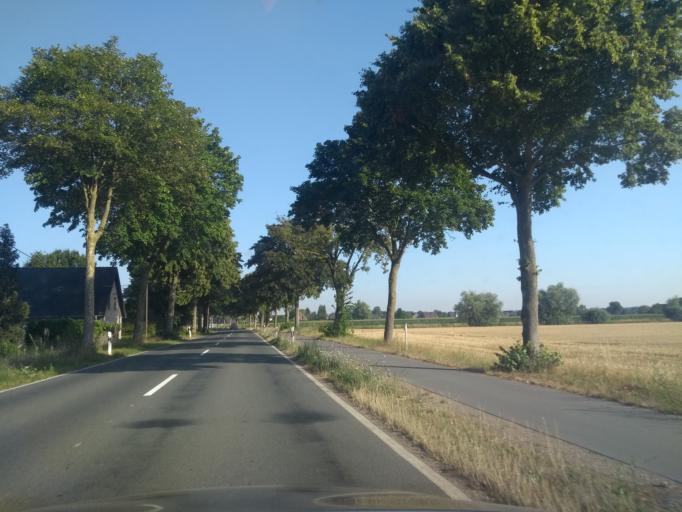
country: DE
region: North Rhine-Westphalia
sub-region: Regierungsbezirk Dusseldorf
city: Kleve
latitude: 51.8228
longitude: 6.1125
